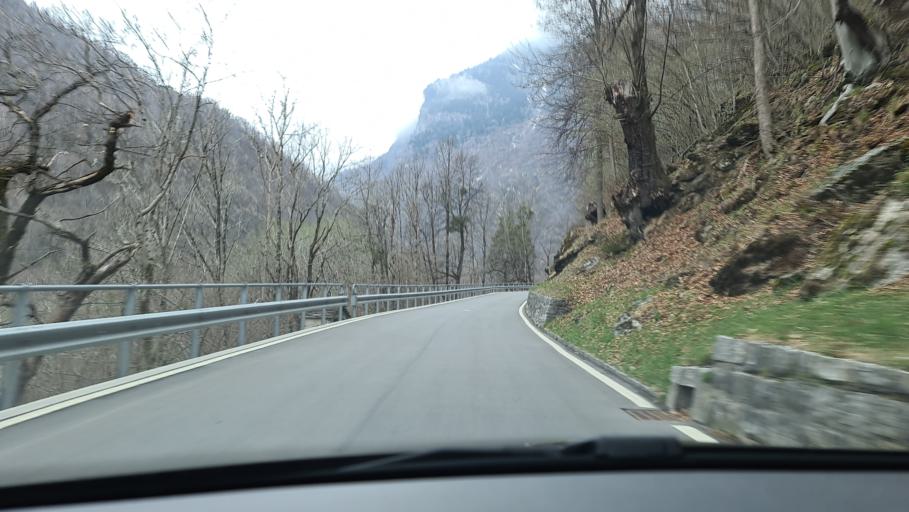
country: CH
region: Ticino
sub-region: Vallemaggia District
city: Cevio
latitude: 46.4024
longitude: 8.6501
